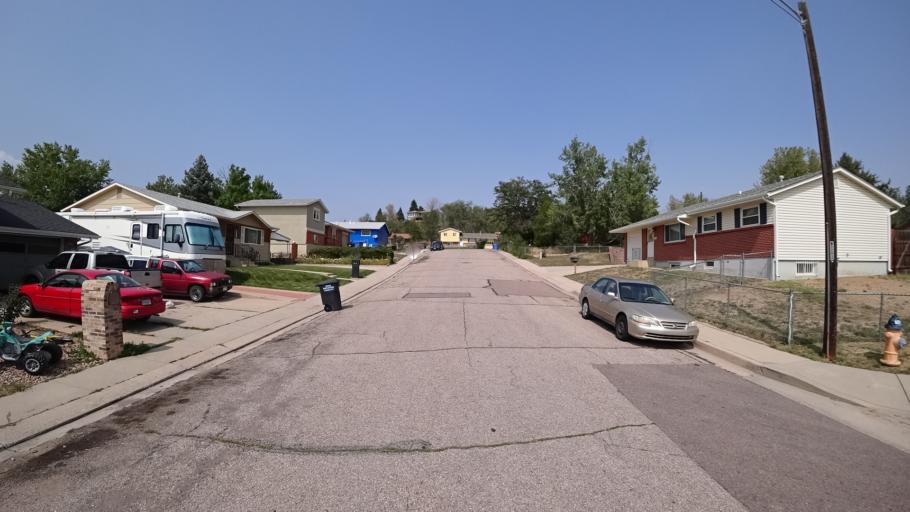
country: US
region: Colorado
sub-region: El Paso County
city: Stratmoor
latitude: 38.7979
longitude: -104.7745
